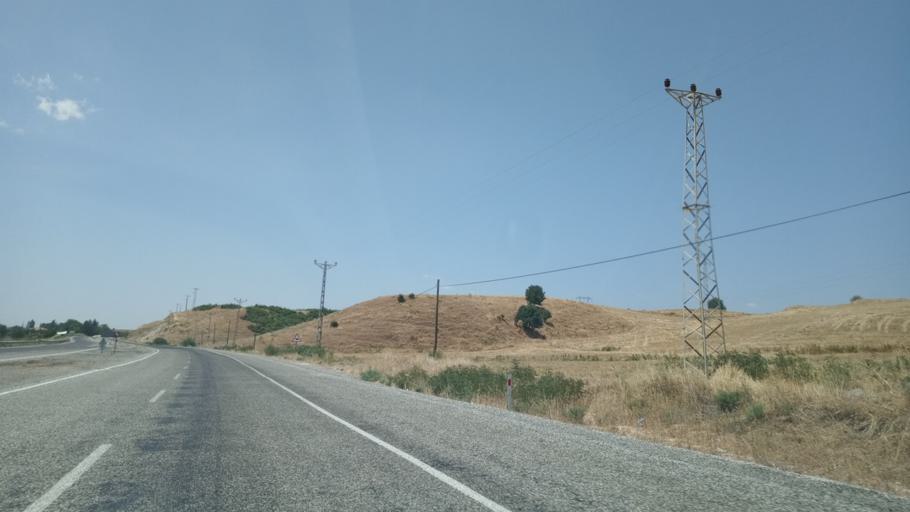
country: TR
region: Batman
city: Bekirhan
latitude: 38.1579
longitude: 41.3367
